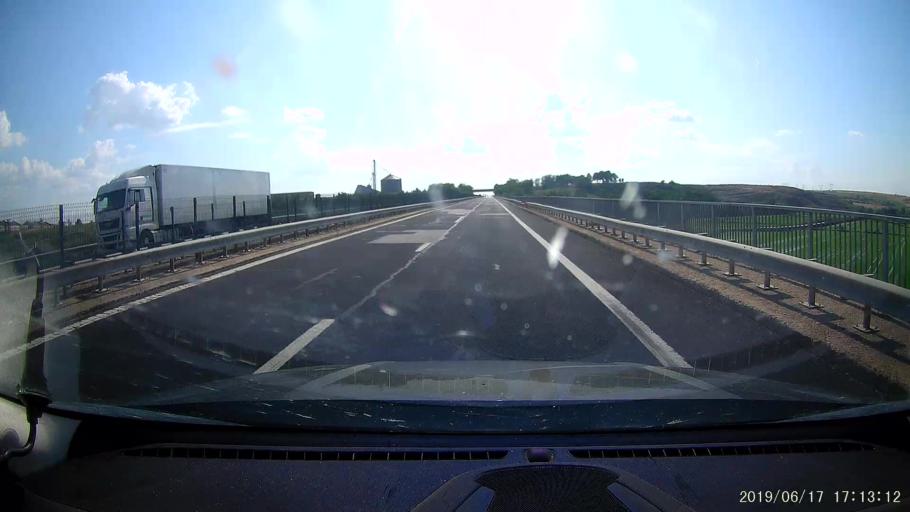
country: TR
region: Edirne
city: Edirne
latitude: 41.7010
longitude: 26.5447
